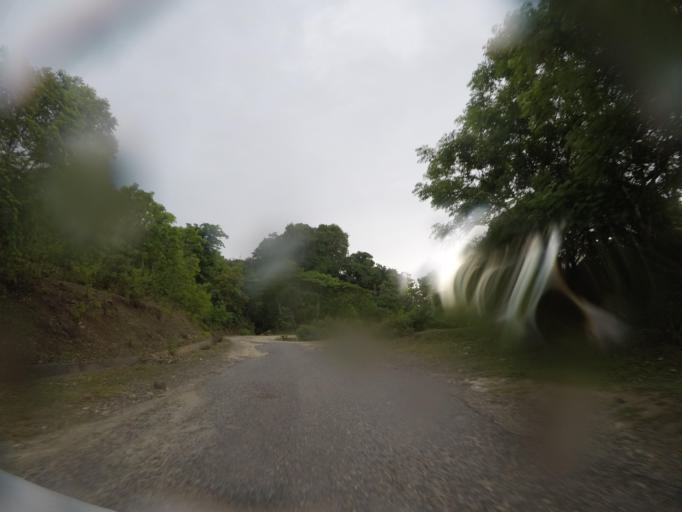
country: TL
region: Bobonaro
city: Maliana
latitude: -8.9634
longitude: 125.0278
